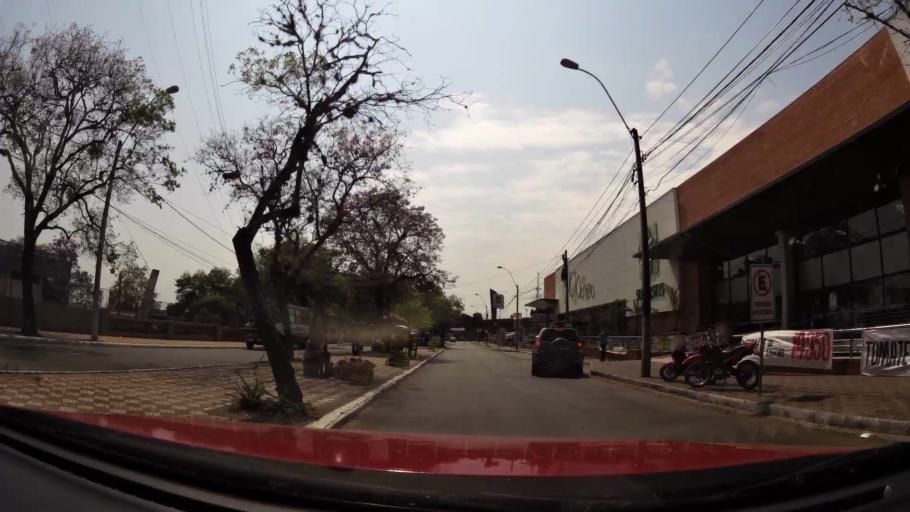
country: PY
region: Asuncion
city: Asuncion
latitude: -25.2880
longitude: -57.6494
